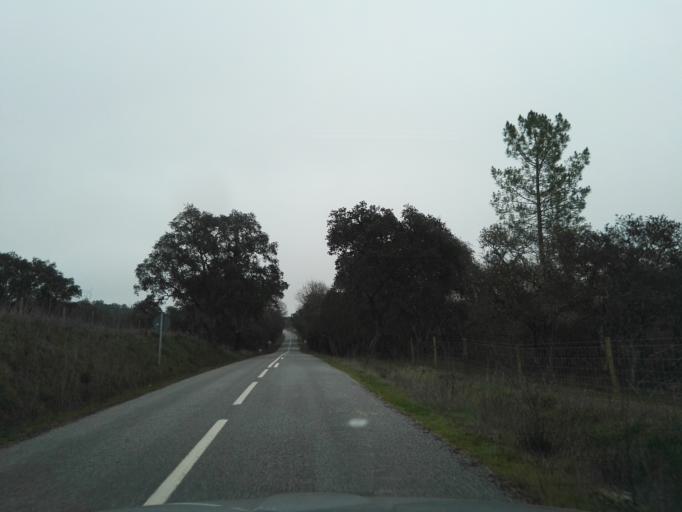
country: PT
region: Evora
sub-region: Vendas Novas
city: Vendas Novas
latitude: 38.7651
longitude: -8.4025
